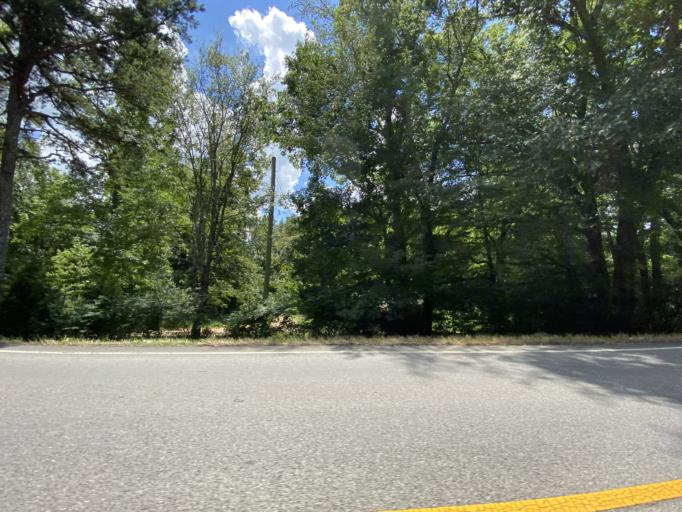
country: US
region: Alabama
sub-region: Lauderdale County
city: Underwood-Petersville
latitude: 34.9584
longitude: -87.8780
